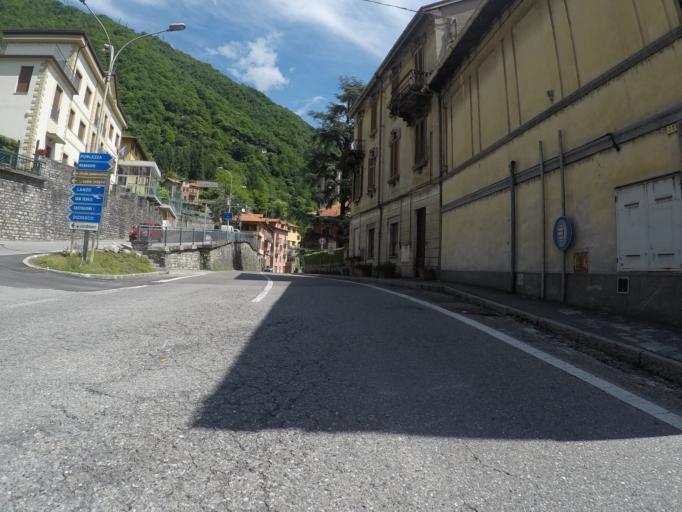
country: IT
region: Lombardy
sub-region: Provincia di Como
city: Argegno
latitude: 45.9447
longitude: 9.1280
